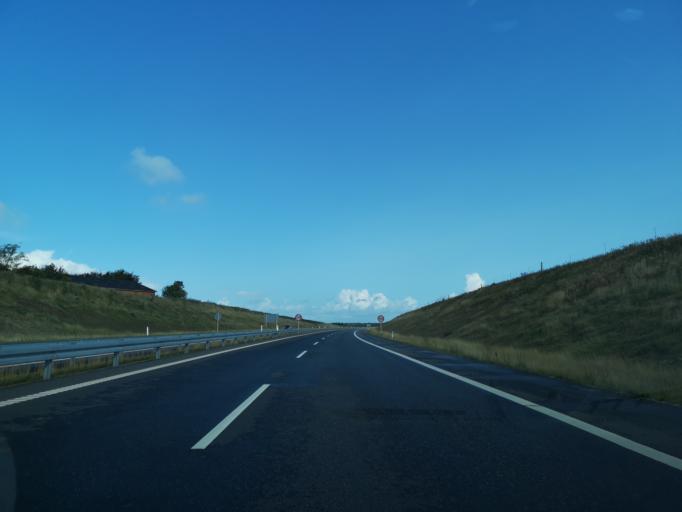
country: DK
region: Central Jutland
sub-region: Herning Kommune
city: Snejbjerg
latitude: 56.1348
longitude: 8.8704
